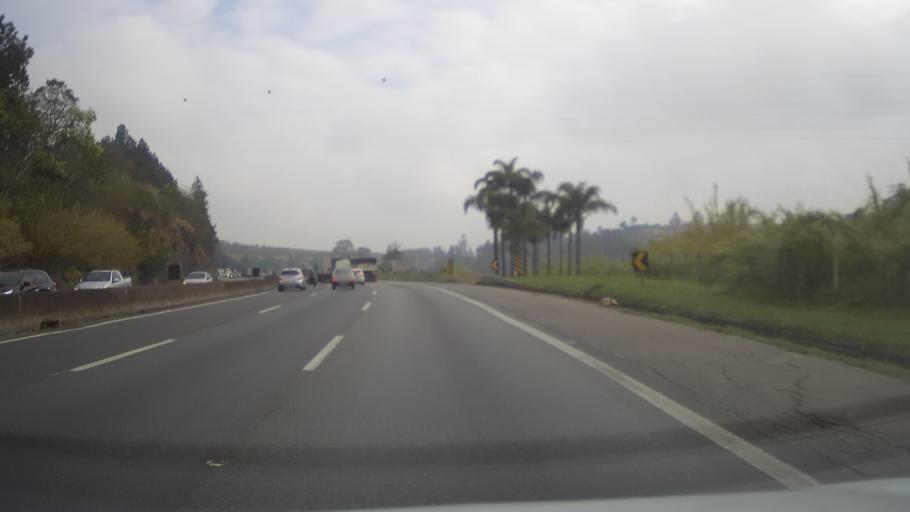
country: BR
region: Sao Paulo
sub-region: Atibaia
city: Atibaia
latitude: -23.0839
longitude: -46.5700
